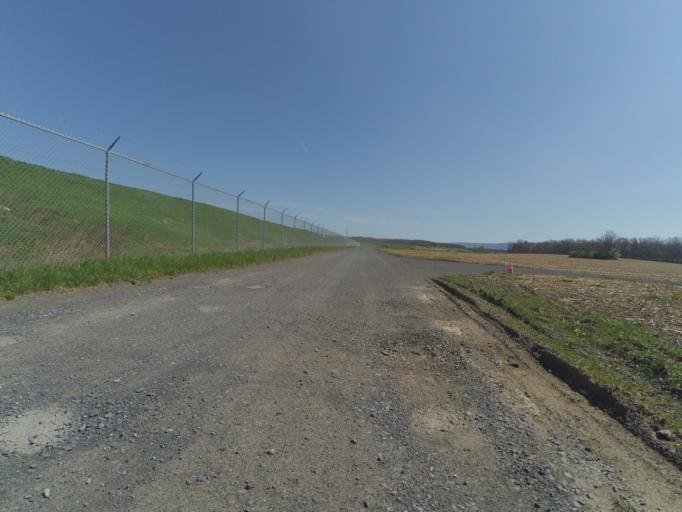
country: US
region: Pennsylvania
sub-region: Centre County
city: Houserville
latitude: 40.8513
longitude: -77.8431
